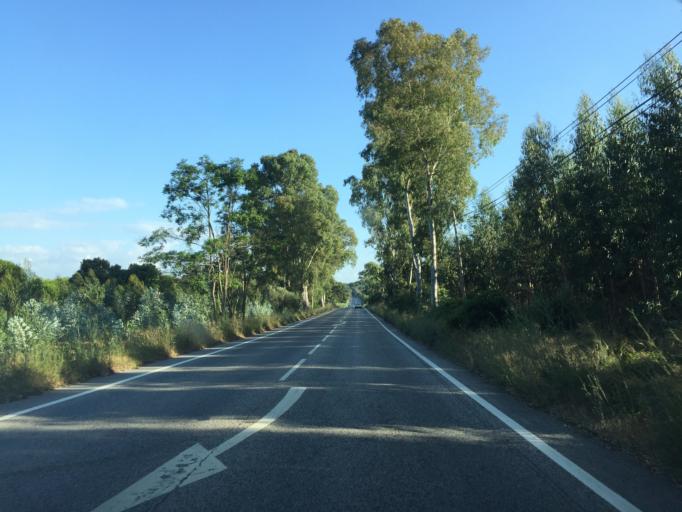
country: PT
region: Lisbon
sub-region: Alenquer
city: Alenquer
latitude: 39.0991
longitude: -8.9918
